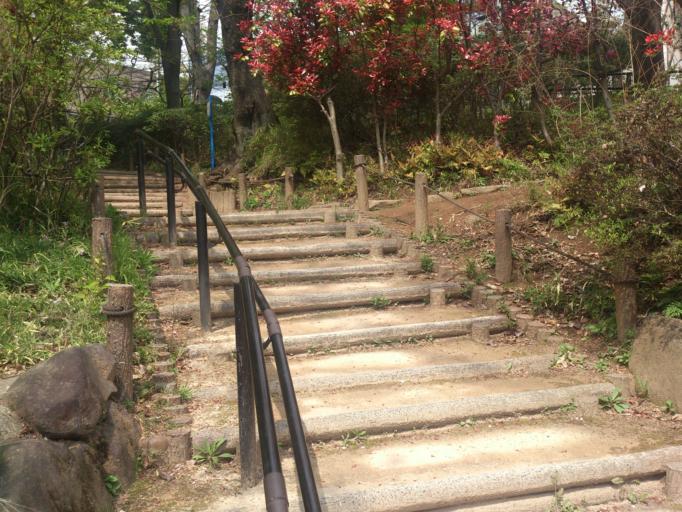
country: JP
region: Tokyo
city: Tokyo
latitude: 35.6599
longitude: 139.6912
